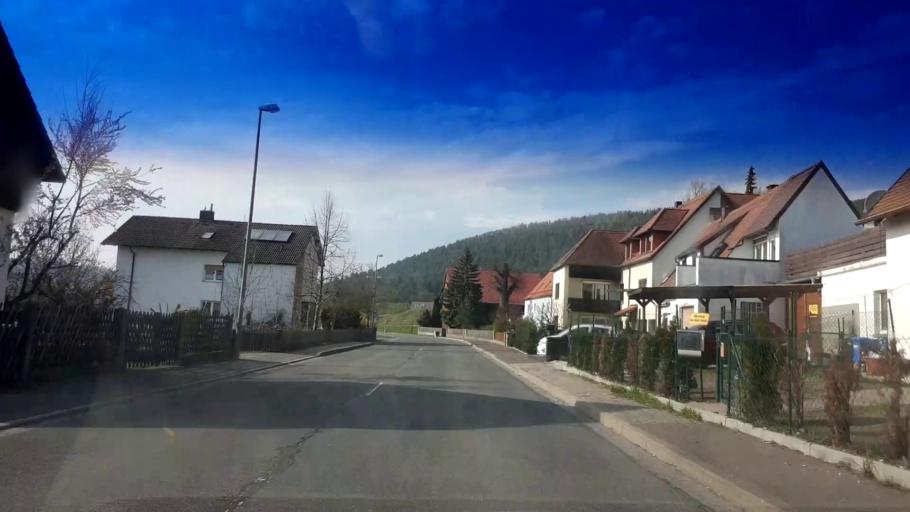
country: DE
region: Bavaria
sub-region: Upper Franconia
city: Harsdorf
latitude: 50.0304
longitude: 11.5640
